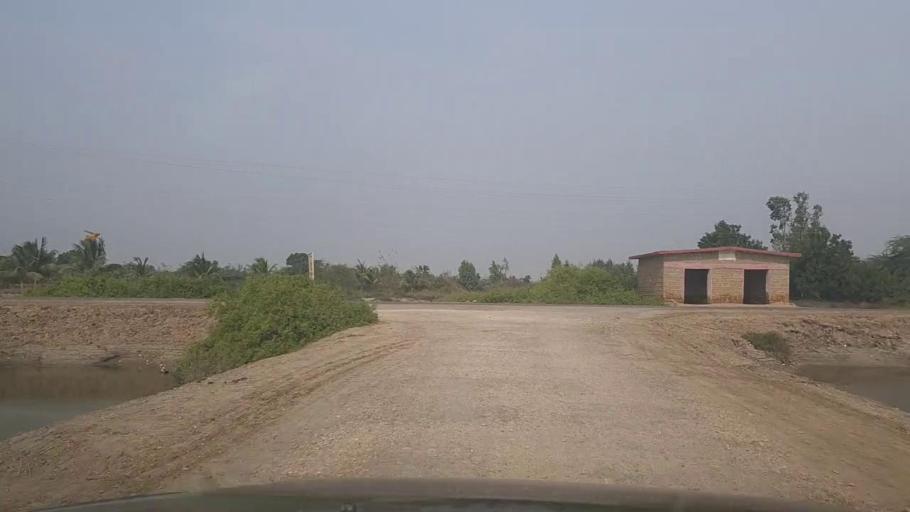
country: PK
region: Sindh
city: Mirpur Sakro
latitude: 24.5741
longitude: 67.7936
